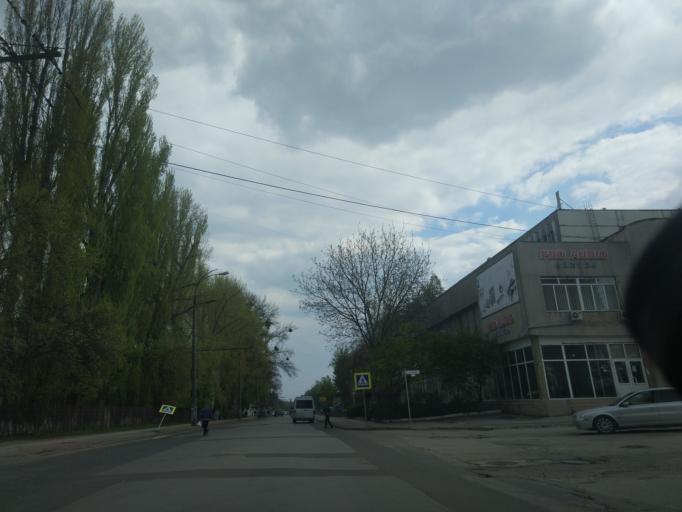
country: MD
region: Chisinau
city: Chisinau
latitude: 46.9854
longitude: 28.8751
